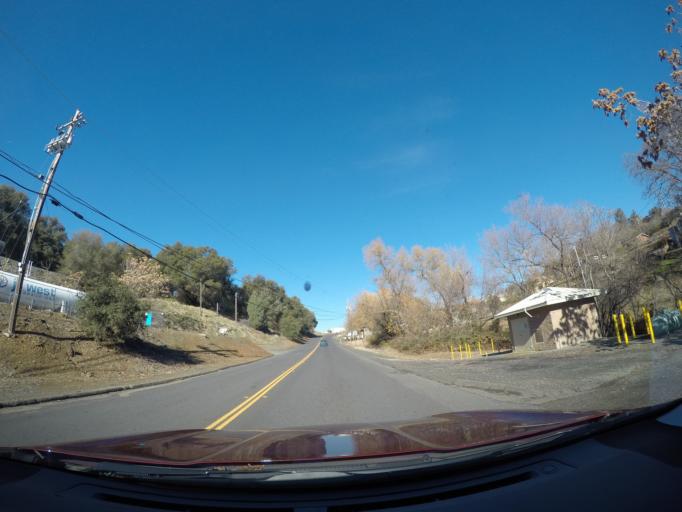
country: US
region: California
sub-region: Tuolumne County
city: Sonora
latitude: 37.9717
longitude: -120.3787
